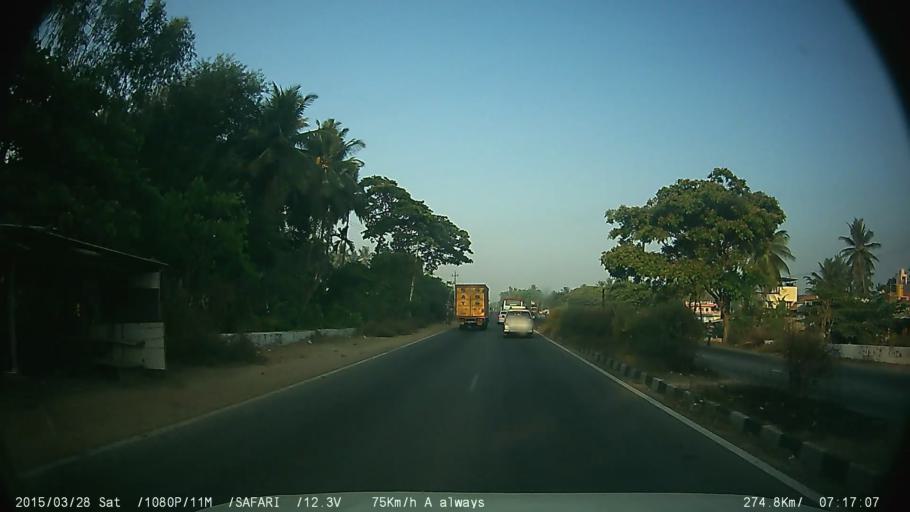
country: IN
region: Karnataka
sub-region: Mandya
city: Mandya
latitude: 12.5073
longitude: 76.8364
